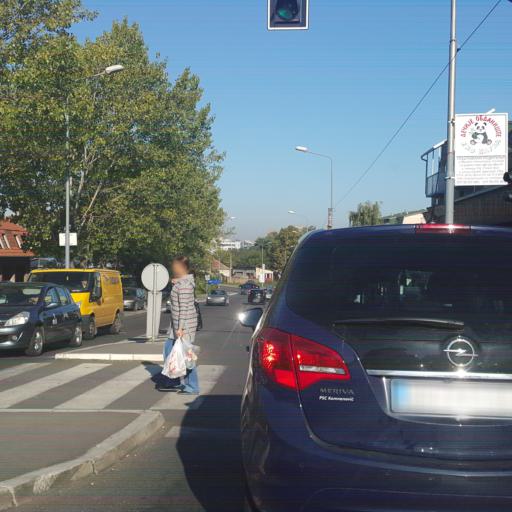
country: RS
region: Central Serbia
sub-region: Belgrade
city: Vozdovac
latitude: 44.7643
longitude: 20.4934
